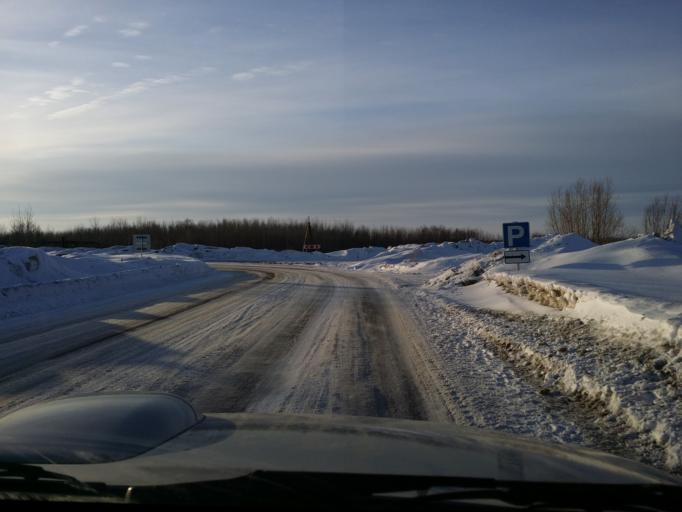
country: RU
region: Khanty-Mansiyskiy Avtonomnyy Okrug
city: Izluchinsk
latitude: 60.9824
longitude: 76.9076
